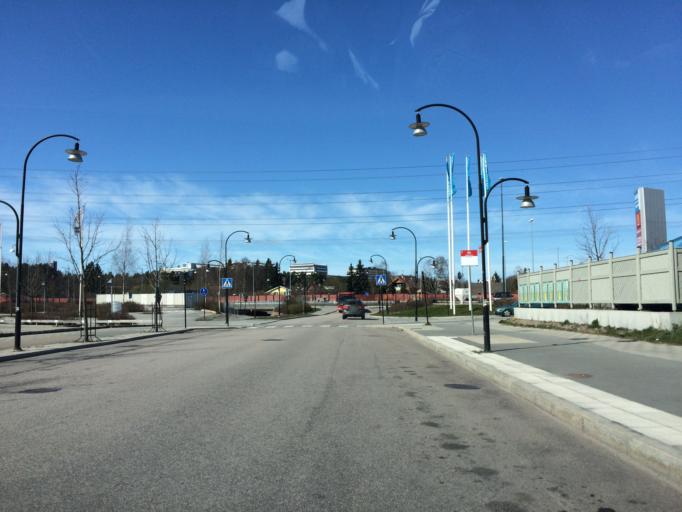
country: SE
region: Stockholm
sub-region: Sollentuna Kommun
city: Sollentuna
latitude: 59.4398
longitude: 17.9333
